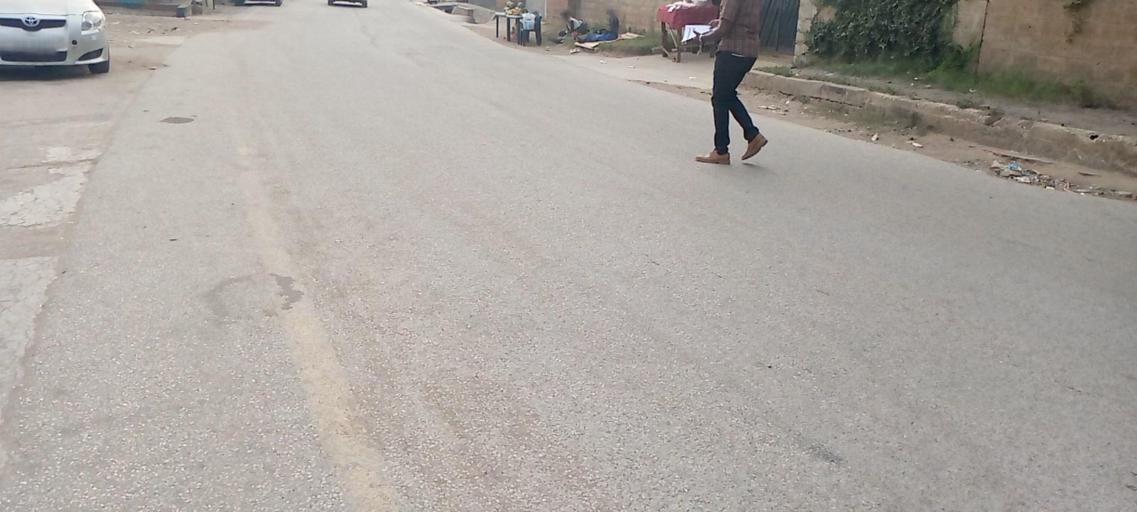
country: ZM
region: Lusaka
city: Lusaka
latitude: -15.4037
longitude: 28.3480
